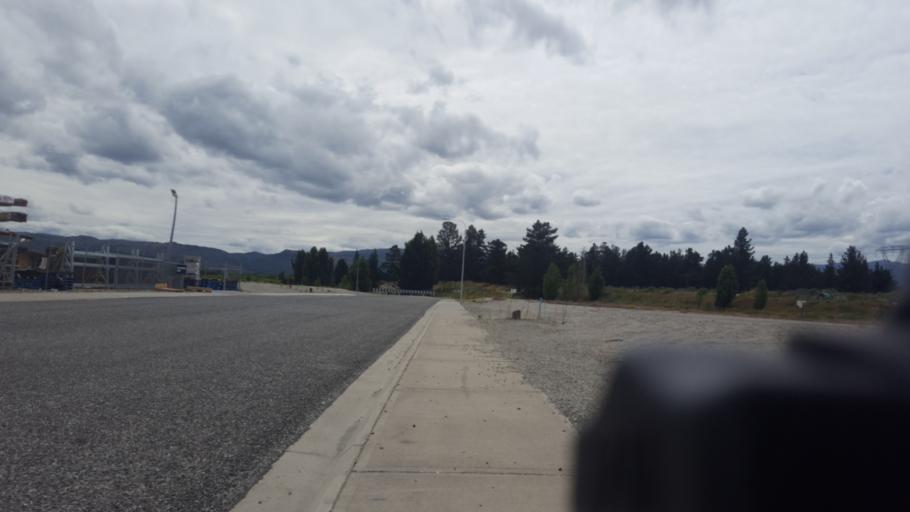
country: NZ
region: Otago
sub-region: Queenstown-Lakes District
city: Wanaka
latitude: -45.2468
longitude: 169.3721
